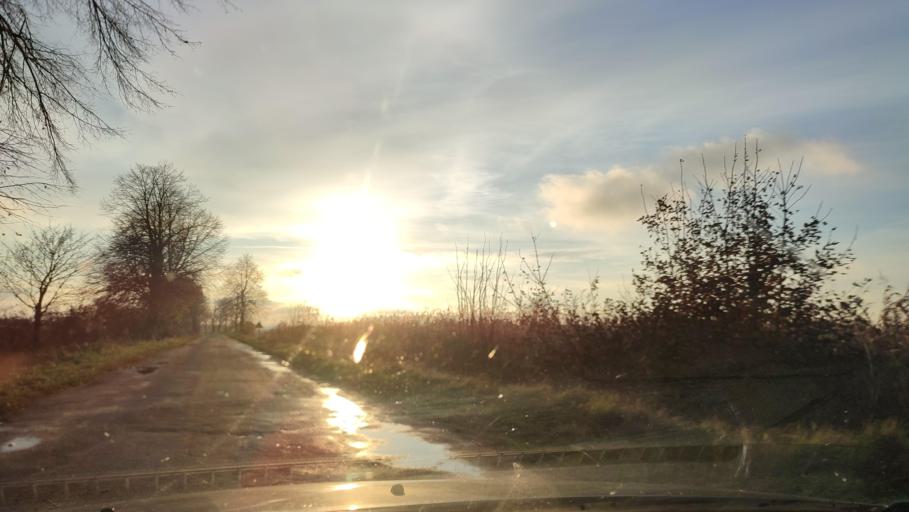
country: PL
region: Masovian Voivodeship
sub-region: Powiat mlawski
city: Wieczfnia Koscielna
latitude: 53.2503
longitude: 20.5858
